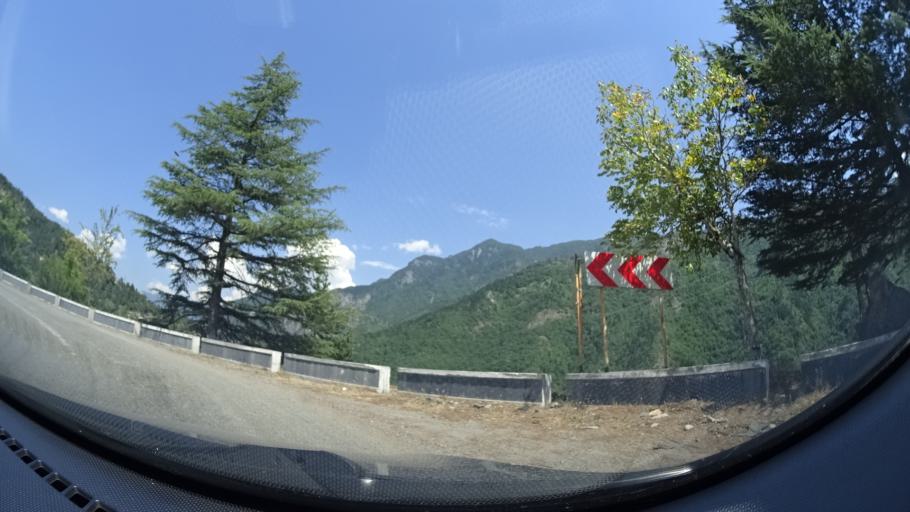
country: GE
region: Ajaria
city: Khulo
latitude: 41.6283
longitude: 42.2970
